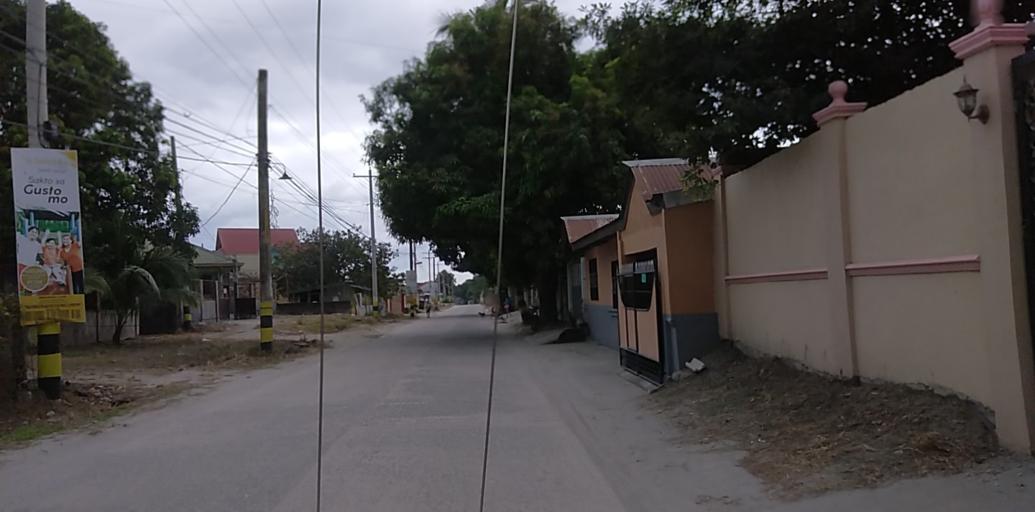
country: PH
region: Central Luzon
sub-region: Province of Pampanga
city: Pio
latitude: 15.0465
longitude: 120.5321
